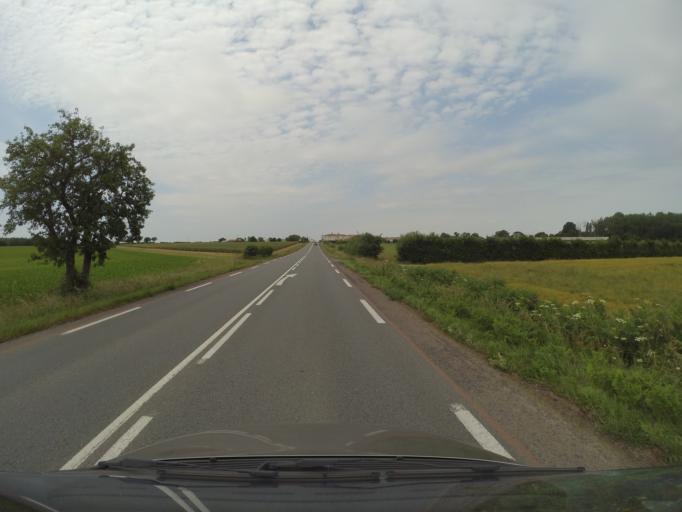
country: FR
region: Pays de la Loire
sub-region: Departement de la Vendee
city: Vendrennes
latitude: 46.8341
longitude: -1.1006
